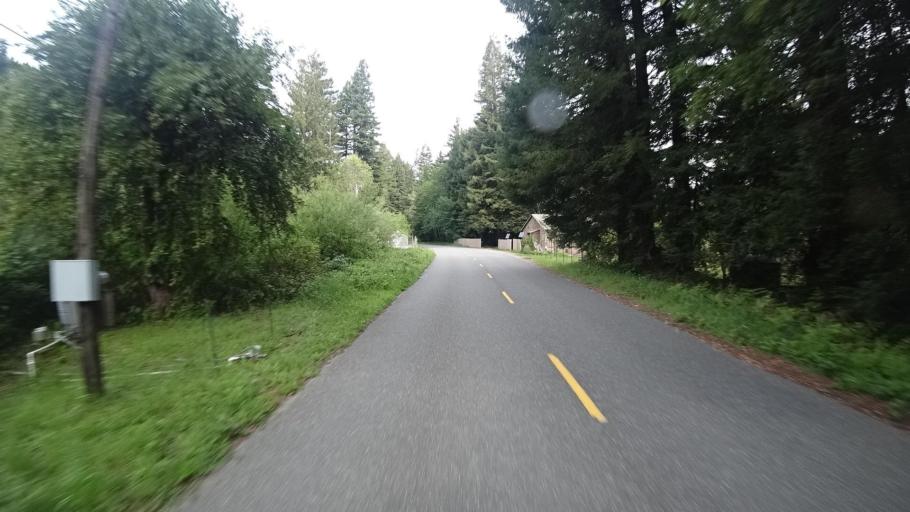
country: US
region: California
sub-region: Humboldt County
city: Redway
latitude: 40.2250
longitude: -123.8272
